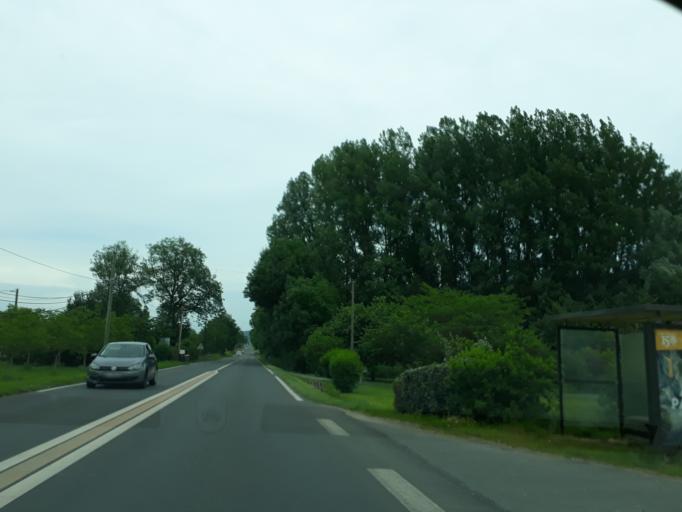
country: FR
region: Limousin
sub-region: Departement de la Correze
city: Cublac
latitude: 45.1275
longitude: 1.3452
